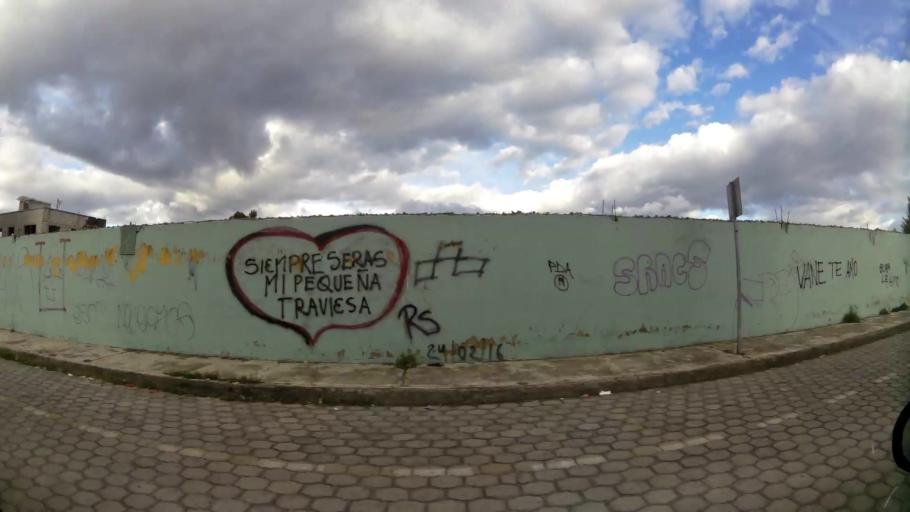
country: EC
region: Pichincha
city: Quito
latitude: -0.1344
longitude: -78.4634
